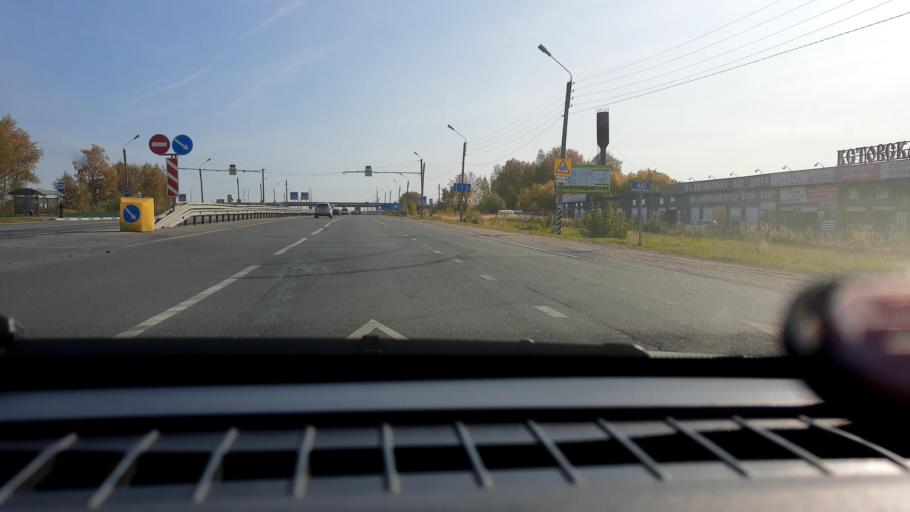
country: RU
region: Nizjnij Novgorod
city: Kstovo
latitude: 56.1299
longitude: 44.2547
